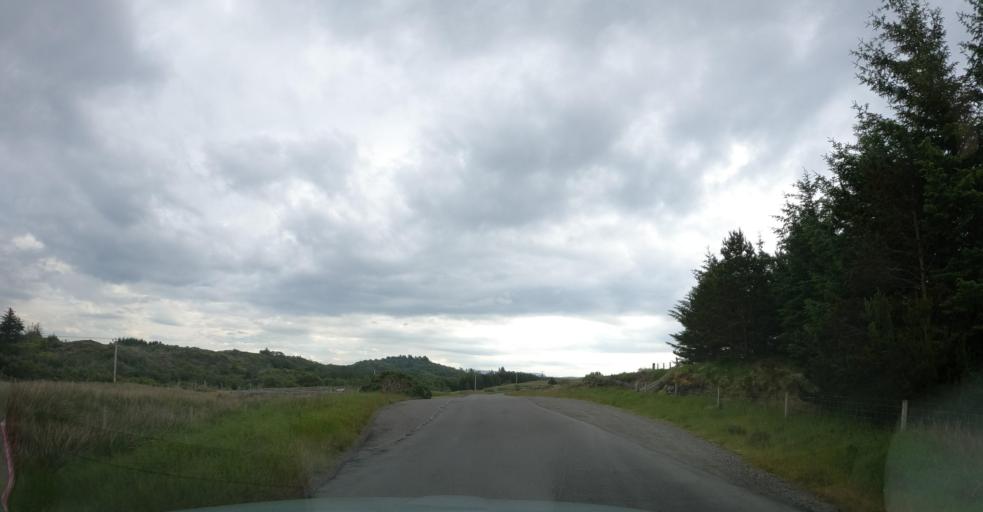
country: GB
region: Scotland
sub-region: Eilean Siar
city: Stornoway
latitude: 58.2030
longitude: -6.4152
